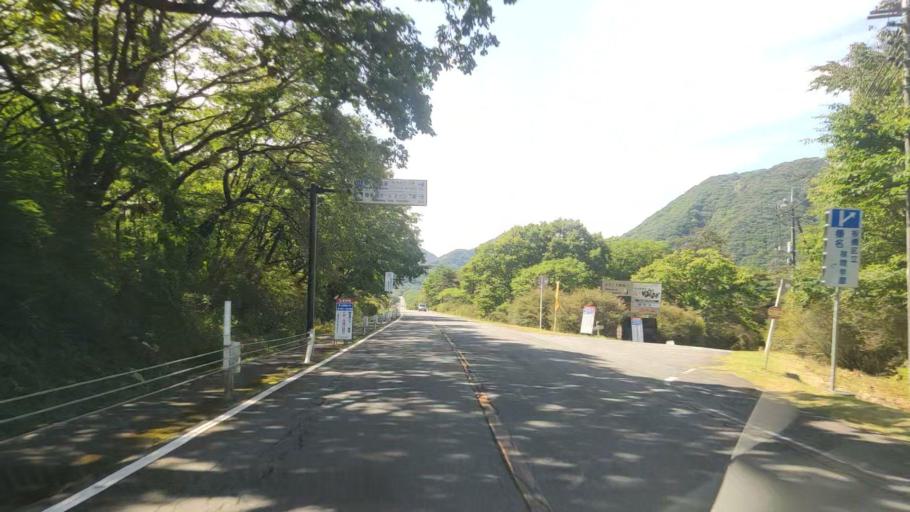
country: JP
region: Gunma
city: Shibukawa
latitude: 36.4799
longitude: 138.8941
